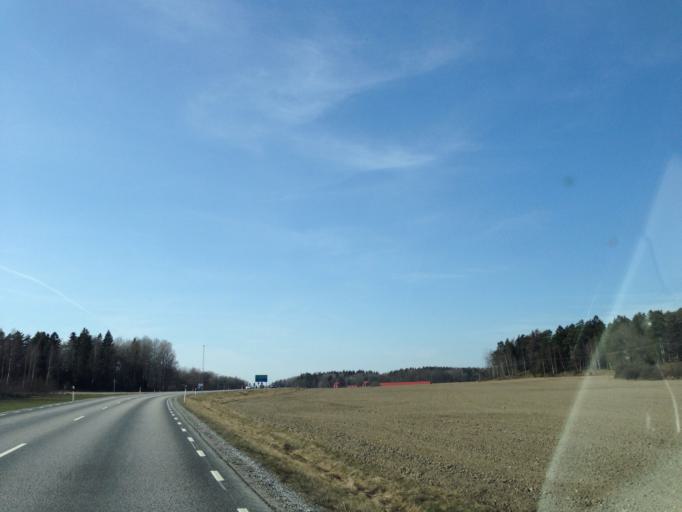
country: SE
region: Stockholm
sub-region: Salems Kommun
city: Ronninge
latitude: 59.2171
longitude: 17.7645
